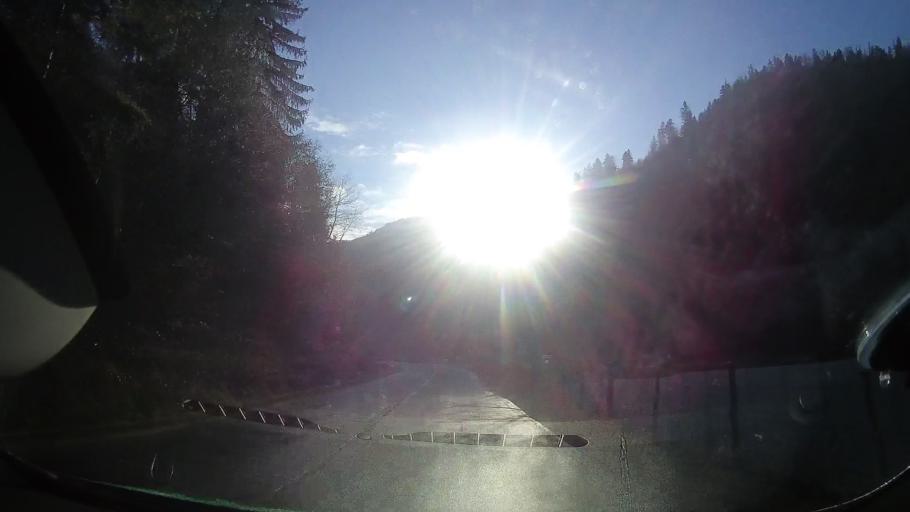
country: RO
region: Alba
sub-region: Comuna Vadu Motilor
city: Vadu Motilor
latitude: 46.3904
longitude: 22.9775
